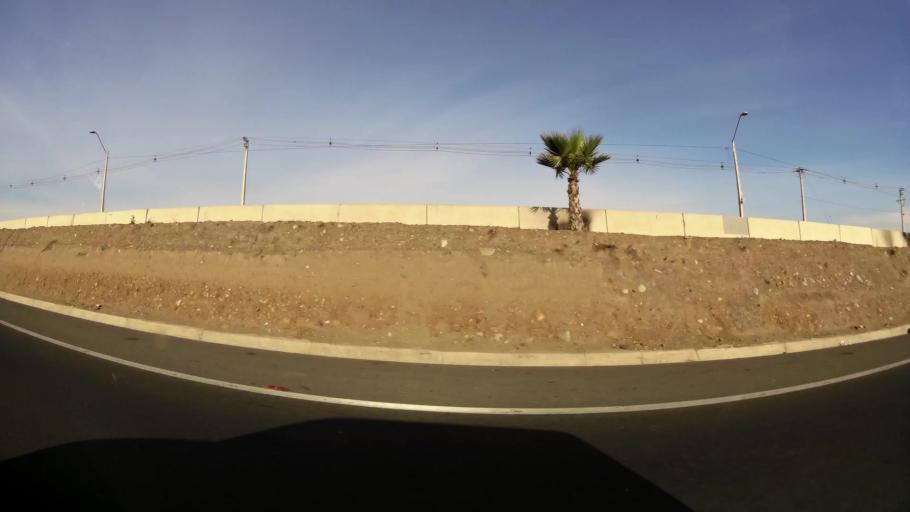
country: CL
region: Santiago Metropolitan
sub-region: Provincia de Santiago
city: La Pintana
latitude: -33.5675
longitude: -70.6132
